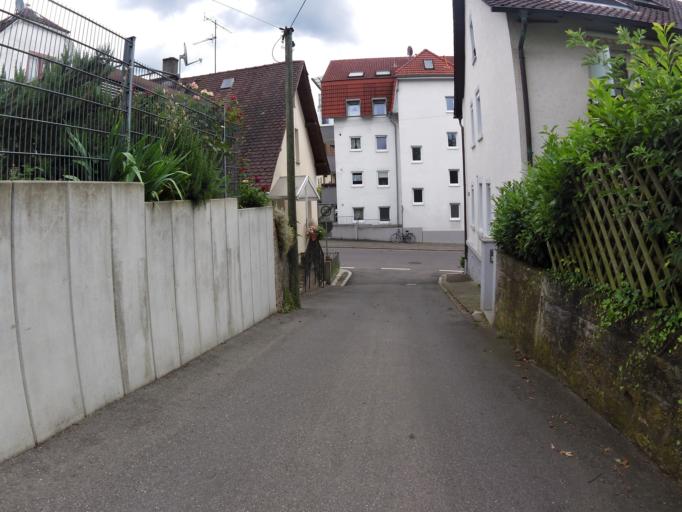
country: DE
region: Baden-Wuerttemberg
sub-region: Freiburg Region
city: Lahr
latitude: 48.3443
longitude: 7.8784
